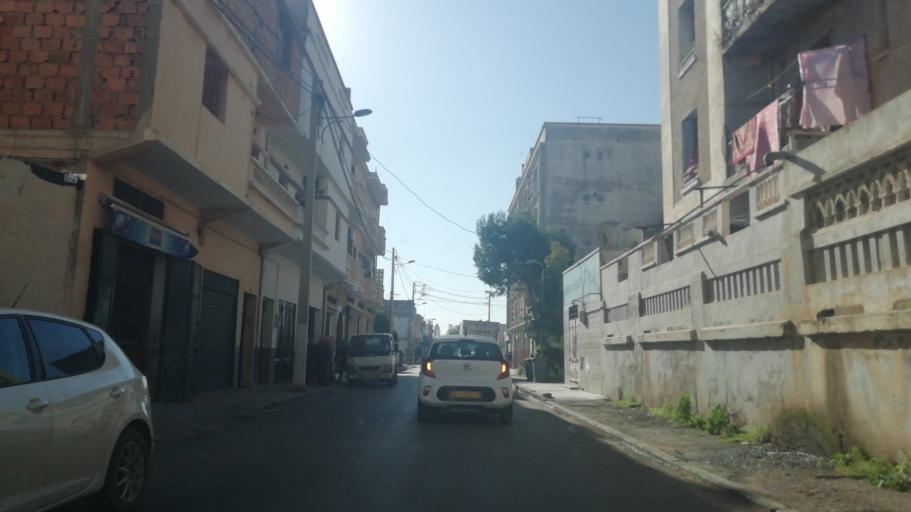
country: DZ
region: Oran
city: Oran
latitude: 35.6809
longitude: -0.6536
